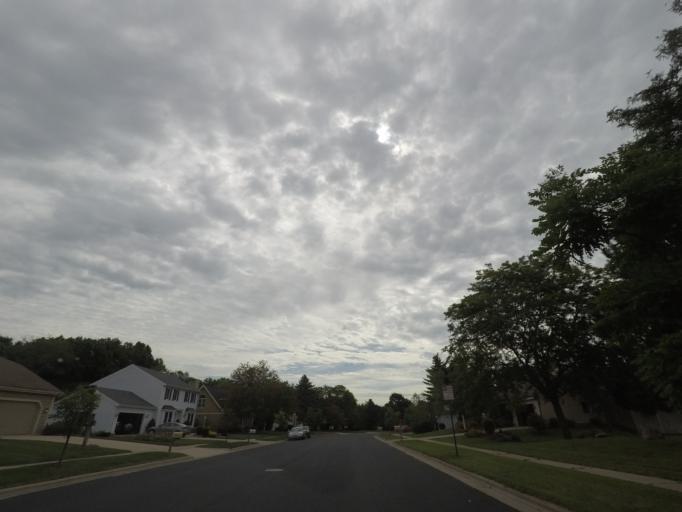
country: US
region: Wisconsin
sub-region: Dane County
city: Middleton
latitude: 43.0894
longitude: -89.4981
